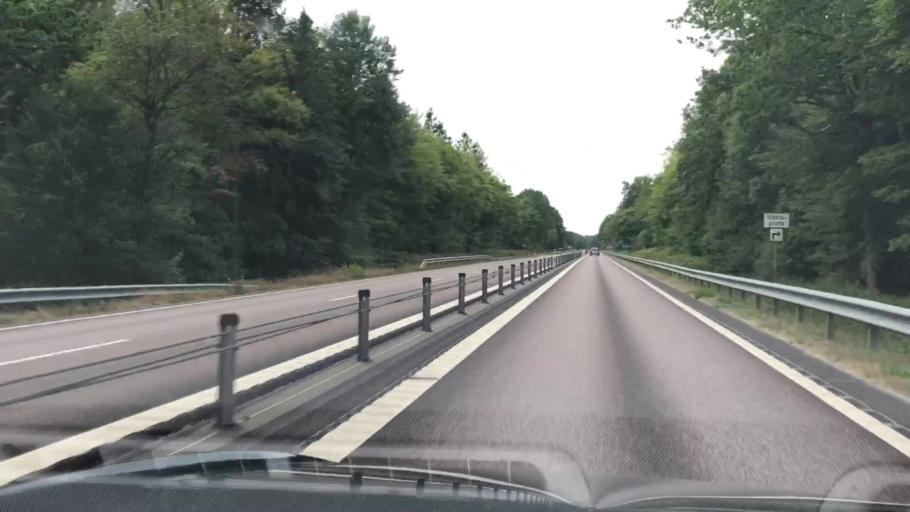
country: SE
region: Blekinge
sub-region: Karlskrona Kommun
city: Jaemjoe
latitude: 56.2343
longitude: 15.9201
